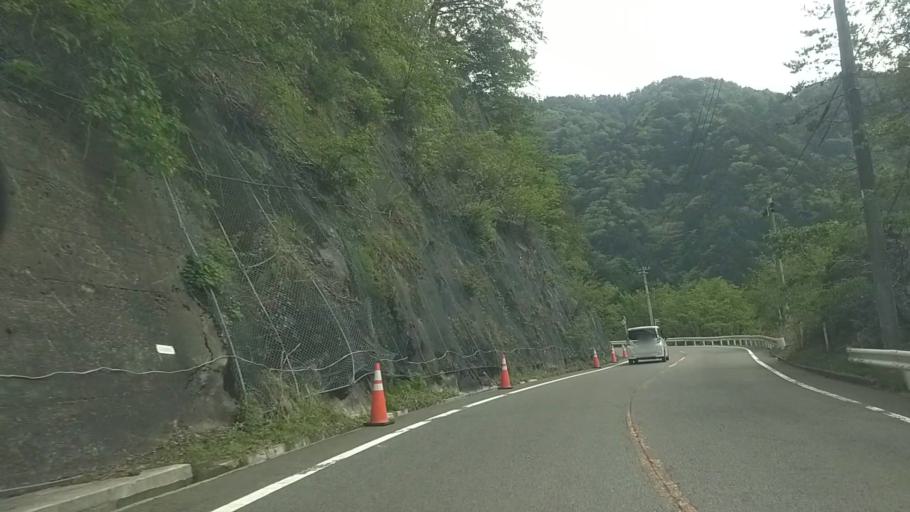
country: JP
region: Yamanashi
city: Fujikawaguchiko
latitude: 35.5100
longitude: 138.6163
